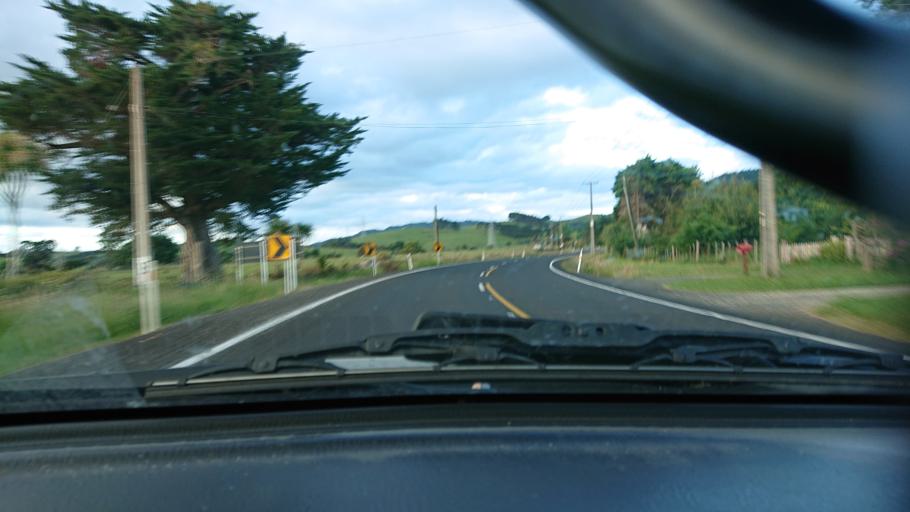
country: NZ
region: Auckland
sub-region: Auckland
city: Parakai
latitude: -36.4895
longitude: 174.4478
